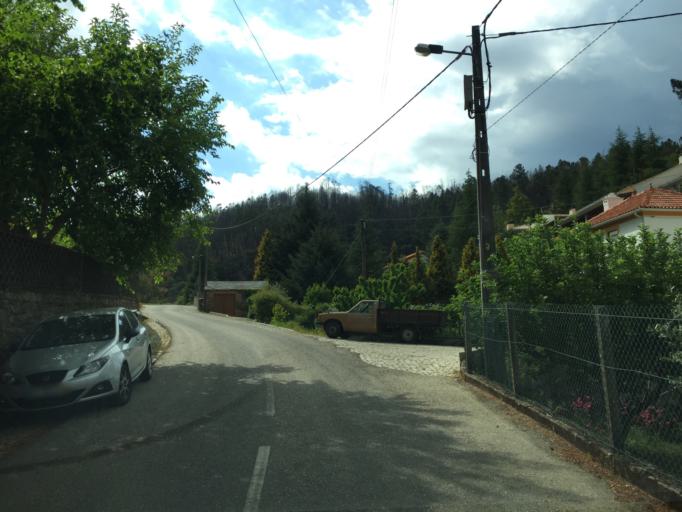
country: PT
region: Coimbra
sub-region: Pampilhosa da Serra
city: Pampilhosa da Serra
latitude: 40.0517
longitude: -8.0246
